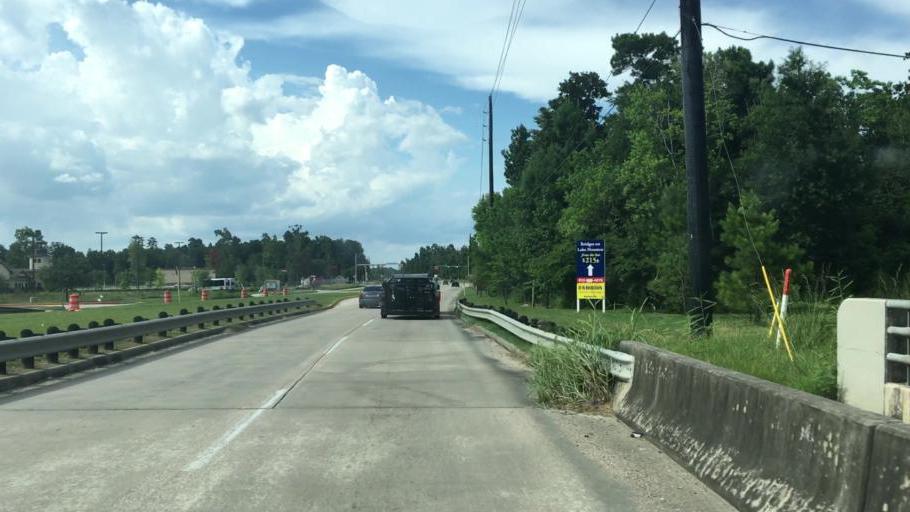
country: US
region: Texas
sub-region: Harris County
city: Atascocita
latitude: 29.9354
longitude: -95.1761
